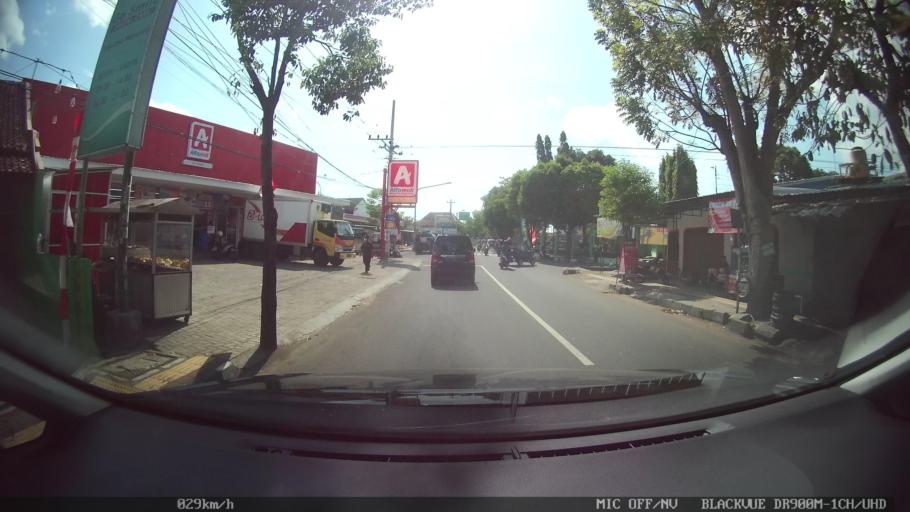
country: ID
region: Daerah Istimewa Yogyakarta
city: Yogyakarta
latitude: -7.8252
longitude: 110.3768
